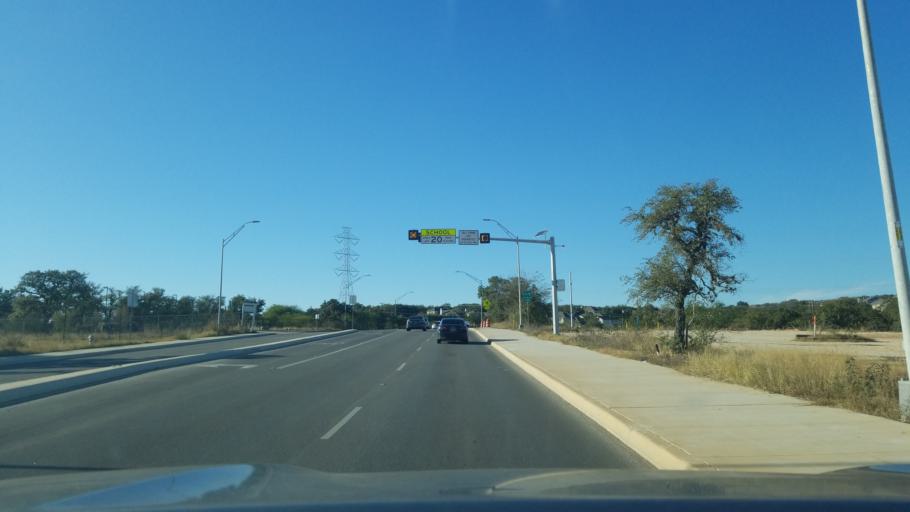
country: US
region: Texas
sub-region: Bexar County
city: Hollywood Park
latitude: 29.6298
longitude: -98.4795
